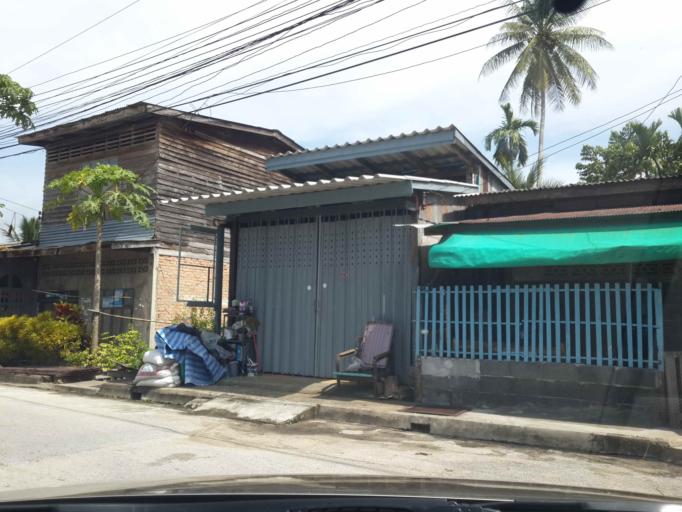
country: TH
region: Narathiwat
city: Rueso
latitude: 6.3966
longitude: 101.5171
